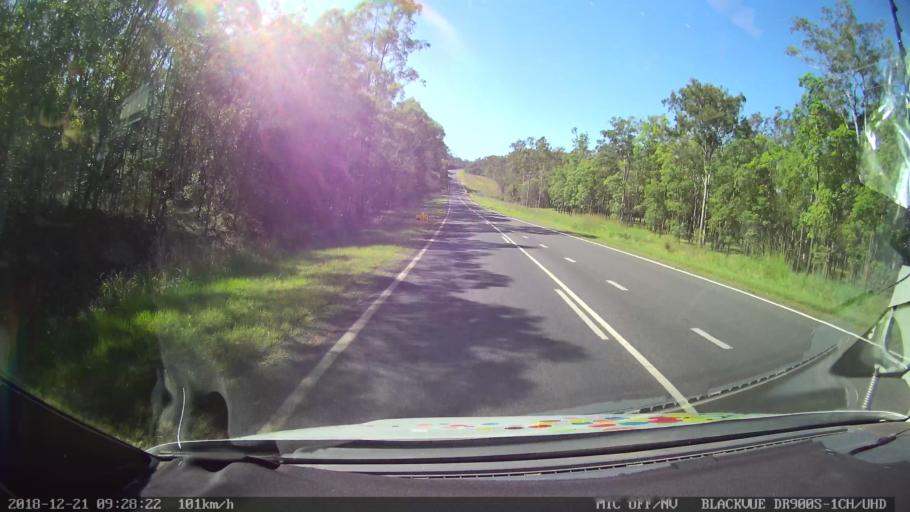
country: AU
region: New South Wales
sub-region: Clarence Valley
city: Maclean
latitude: -29.4164
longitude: 152.9865
